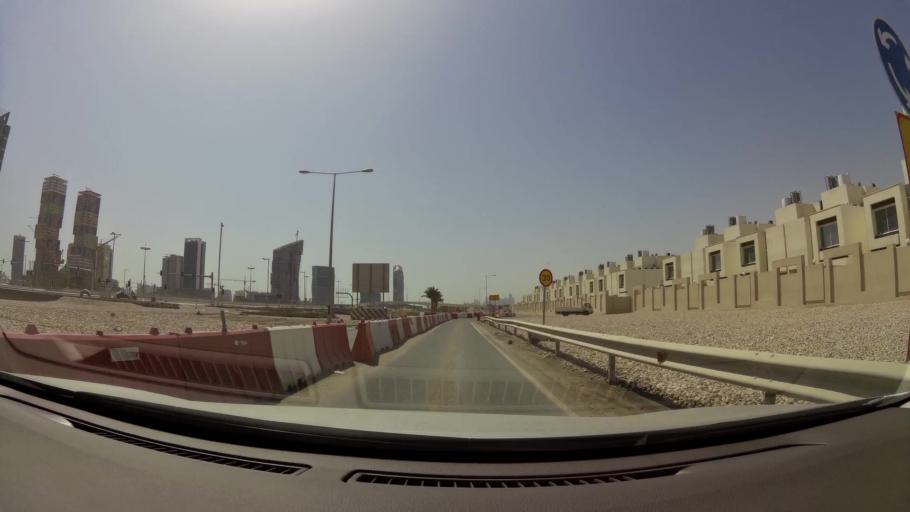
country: QA
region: Baladiyat ad Dawhah
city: Doha
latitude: 25.3889
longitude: 51.5175
